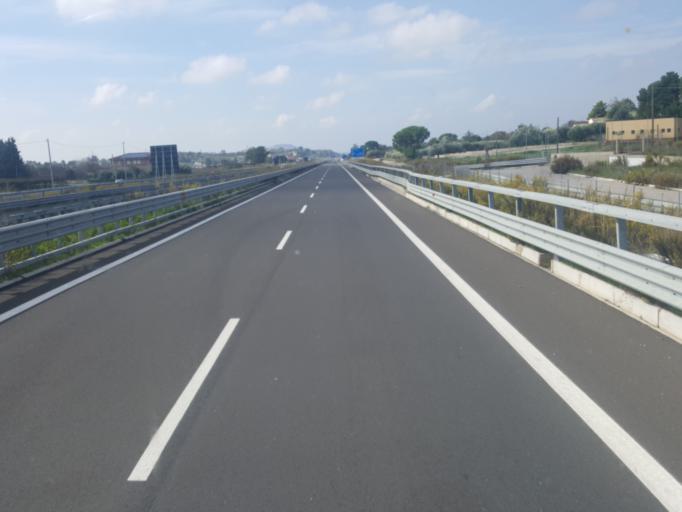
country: IT
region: Sicily
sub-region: Agrigento
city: Racalmuto
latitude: 37.3817
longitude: 13.7311
